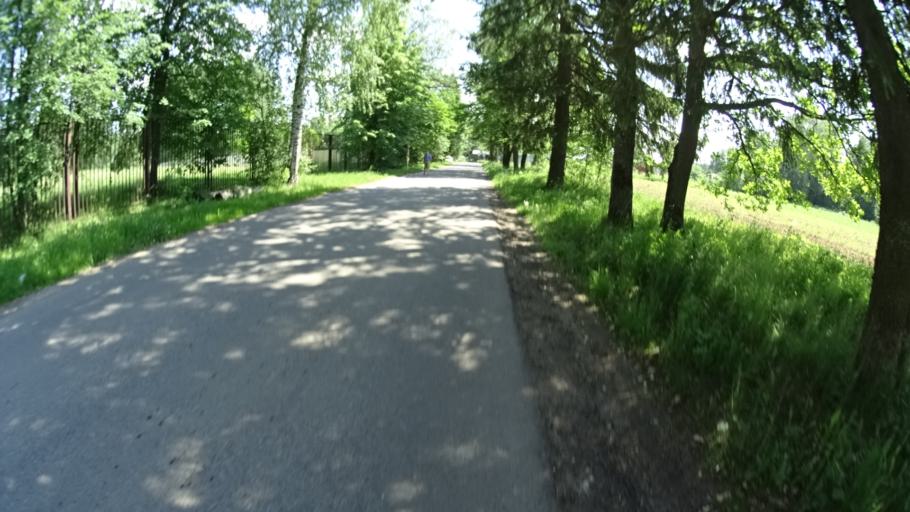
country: RU
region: Moskovskaya
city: Lesnoy
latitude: 56.0692
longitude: 37.9874
